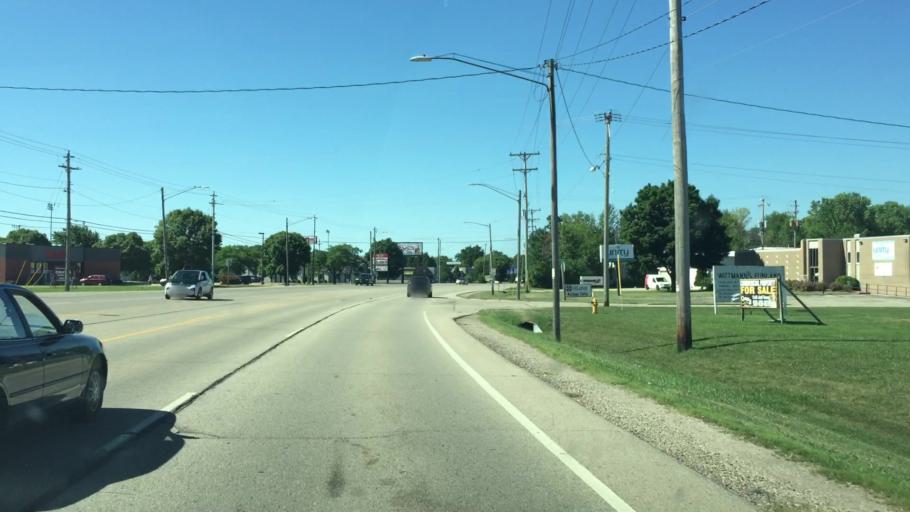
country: US
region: Wisconsin
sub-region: Winnebago County
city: Menasha
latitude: 44.2272
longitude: -88.4242
